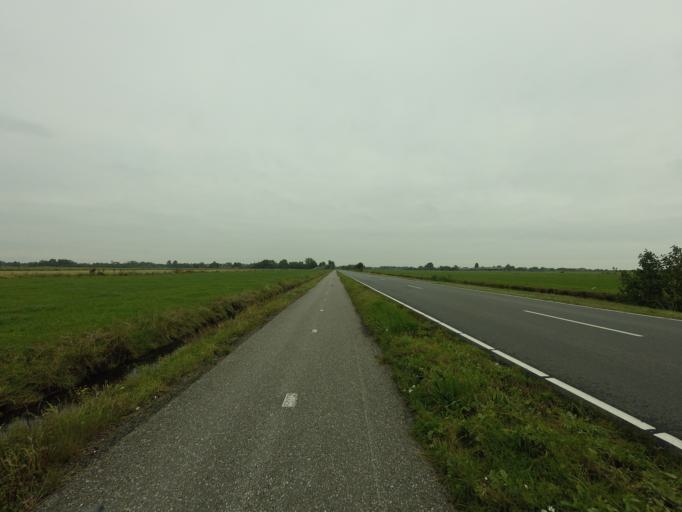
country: NL
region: Utrecht
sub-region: Gemeente Woerden
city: Woerden
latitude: 52.1414
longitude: 4.8609
